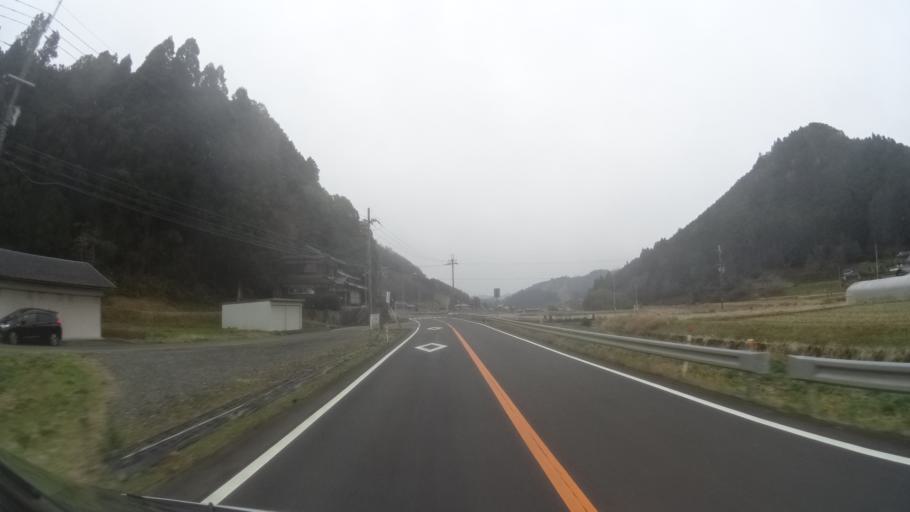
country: JP
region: Kyoto
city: Ayabe
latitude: 35.2106
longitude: 135.3487
